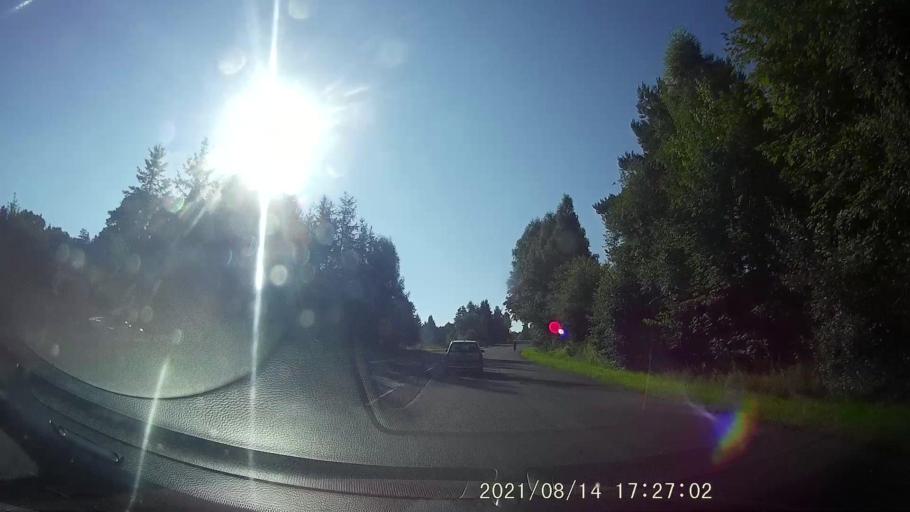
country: PL
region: Lower Silesian Voivodeship
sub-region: Jelenia Gora
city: Jelenia Gora
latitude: 50.9074
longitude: 15.7104
